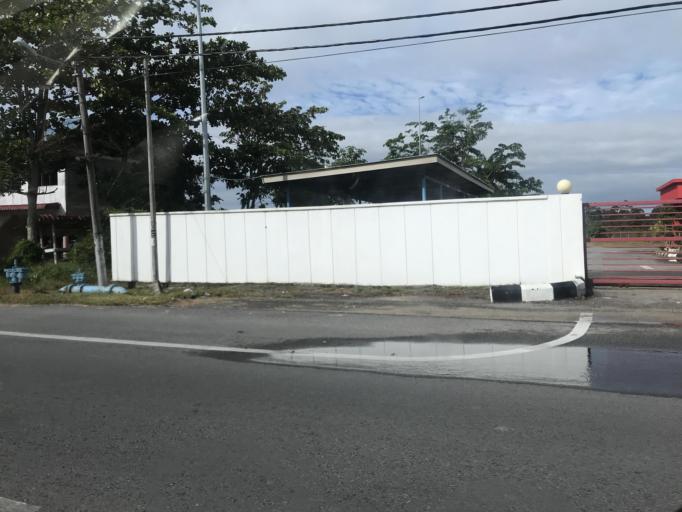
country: MY
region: Kelantan
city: Kota Bharu
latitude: 6.1236
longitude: 102.1840
